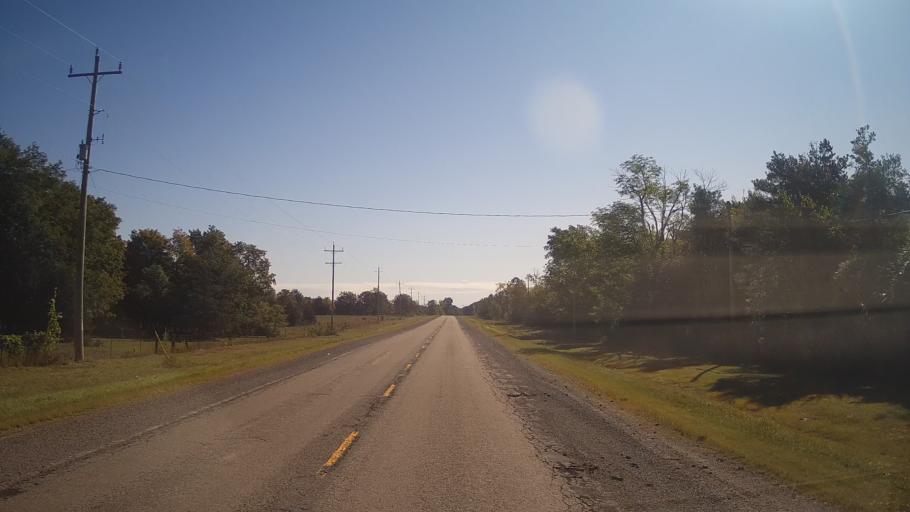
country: CA
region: Ontario
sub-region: Lanark County
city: Smiths Falls
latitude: 44.6269
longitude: -76.0236
